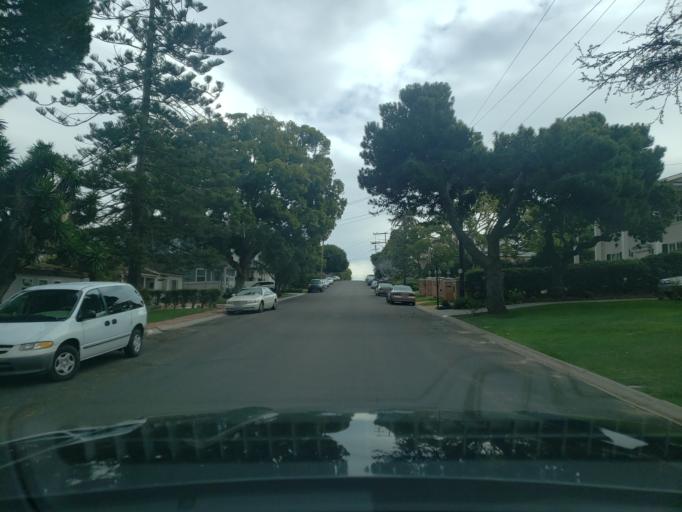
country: US
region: California
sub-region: San Diego County
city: Coronado
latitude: 32.7191
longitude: -117.2457
